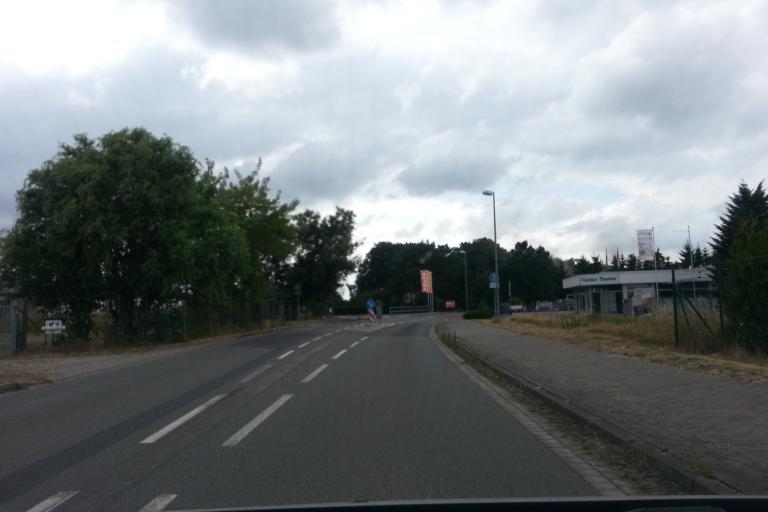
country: DE
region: Mecklenburg-Vorpommern
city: Ferdinandshof
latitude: 53.6583
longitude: 13.8786
